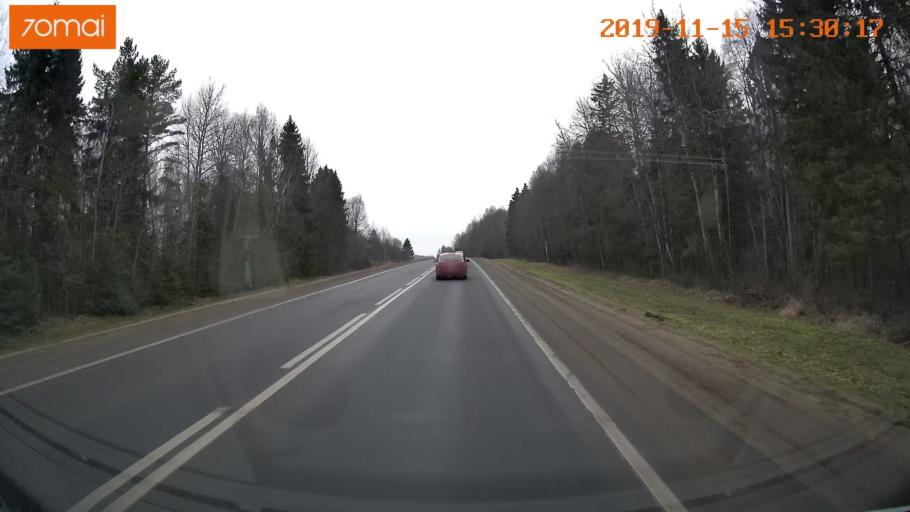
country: RU
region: Jaroslavl
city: Danilov
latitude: 58.1116
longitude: 40.1140
